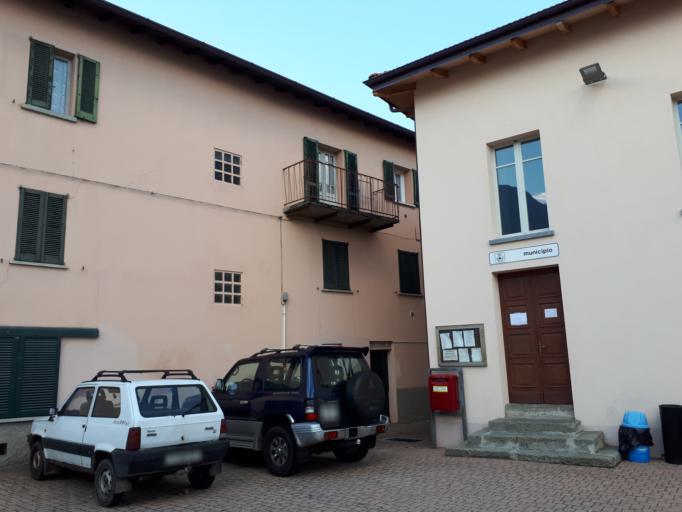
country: IT
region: Lombardy
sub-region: Provincia di Como
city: Stazzona
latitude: 46.1349
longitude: 9.2648
